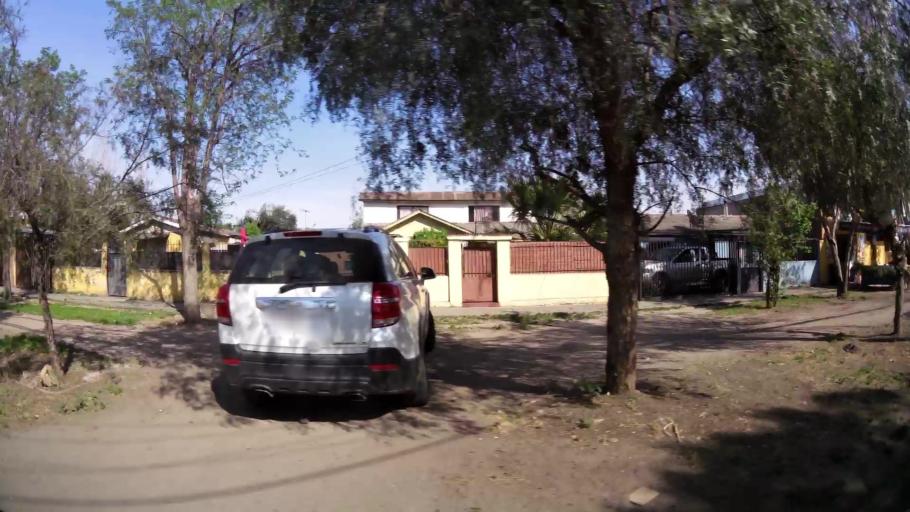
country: CL
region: Santiago Metropolitan
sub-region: Provincia de Santiago
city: Lo Prado
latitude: -33.4323
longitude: -70.7377
